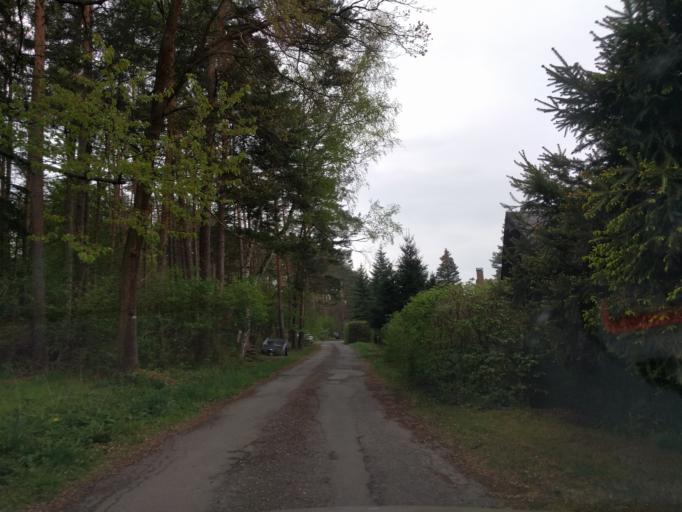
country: CZ
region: Central Bohemia
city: Krasna Hora nad Vltavou
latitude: 49.6675
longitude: 14.2613
